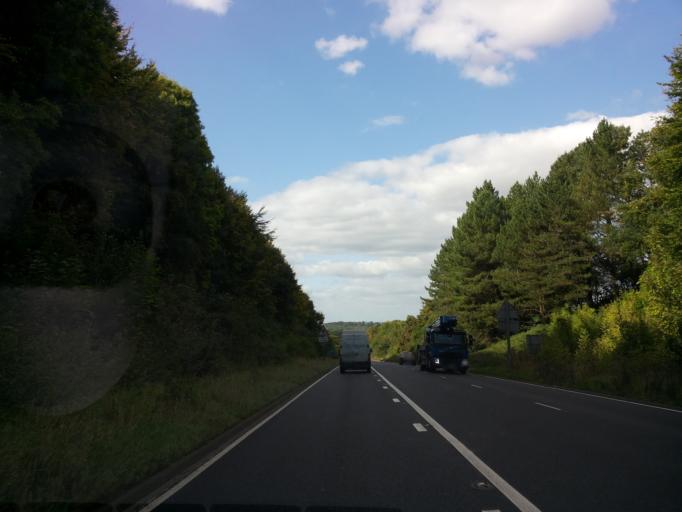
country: GB
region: England
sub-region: Wiltshire
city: Chapmanslade
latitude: 51.2365
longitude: -2.2402
